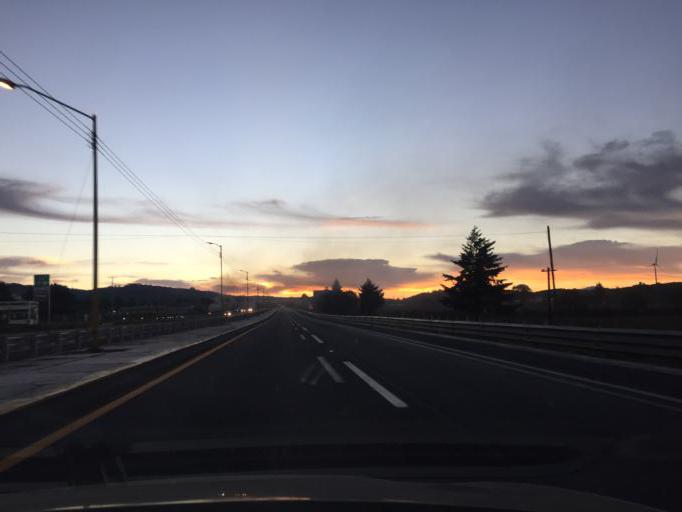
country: MX
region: Puebla
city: San Jose Esperanza
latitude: 18.8644
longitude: -97.3723
